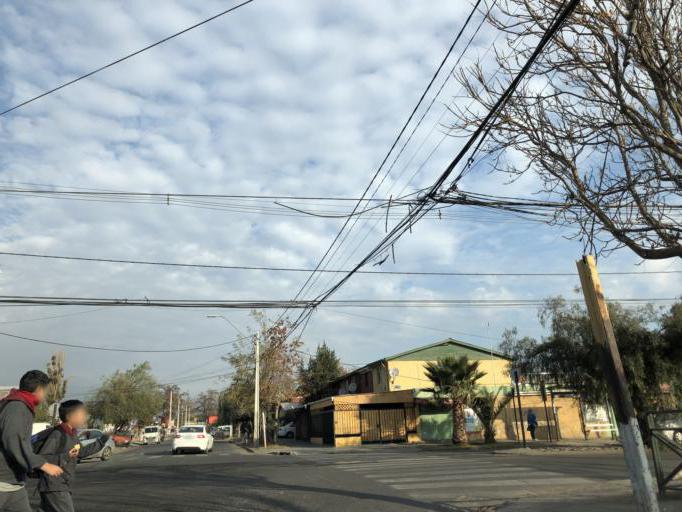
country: CL
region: Santiago Metropolitan
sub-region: Provincia de Cordillera
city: Puente Alto
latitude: -33.6042
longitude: -70.5648
